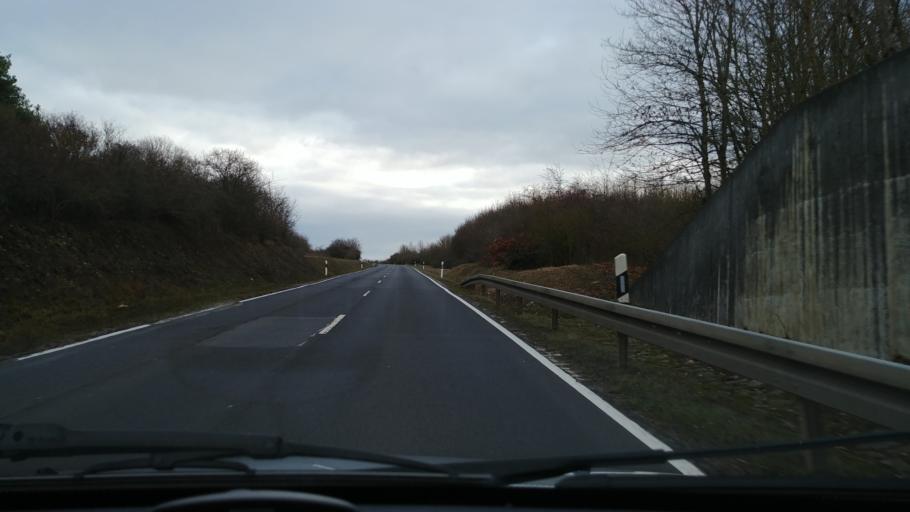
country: DE
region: Bavaria
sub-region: Regierungsbezirk Unterfranken
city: Steinfeld
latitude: 49.9855
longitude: 9.7012
